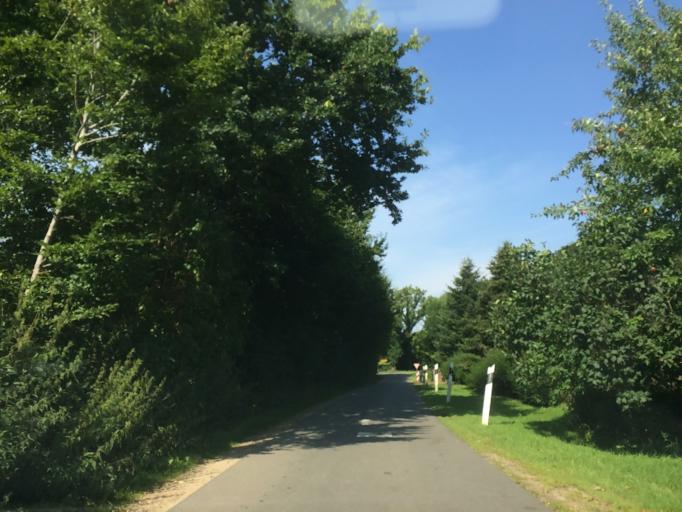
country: DE
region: Schleswig-Holstein
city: Altenhof
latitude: 54.4193
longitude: 9.8926
